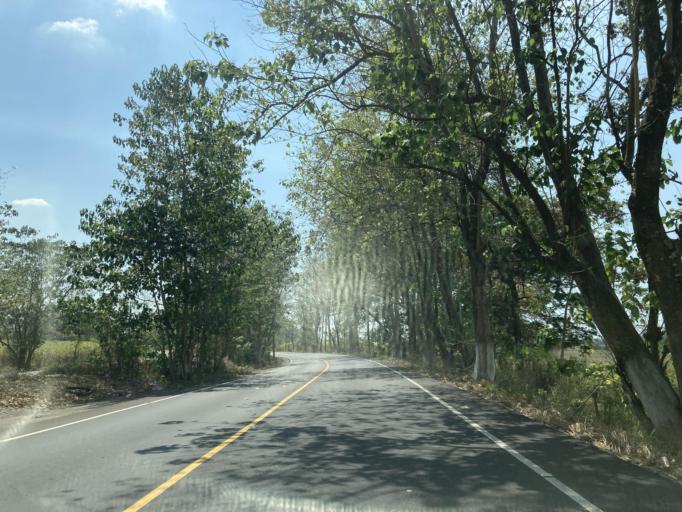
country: GT
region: Escuintla
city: Guanagazapa
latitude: 14.1918
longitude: -90.6956
